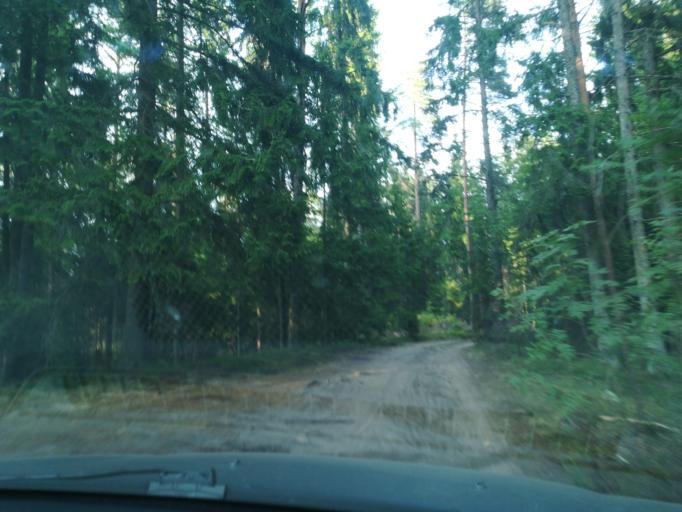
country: RU
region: Leningrad
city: Ust'-Luga
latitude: 59.6777
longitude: 28.2279
